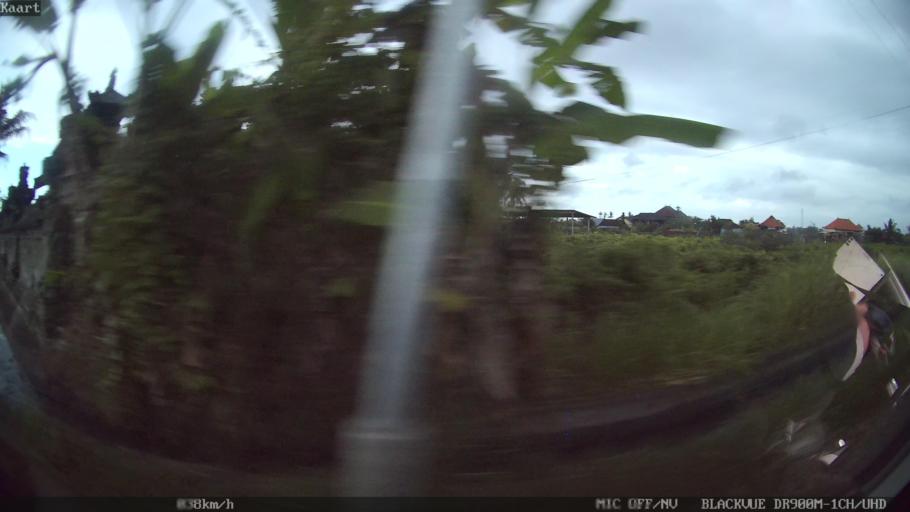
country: ID
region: Bali
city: Banjar Pasekan
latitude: -8.6141
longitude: 115.2948
